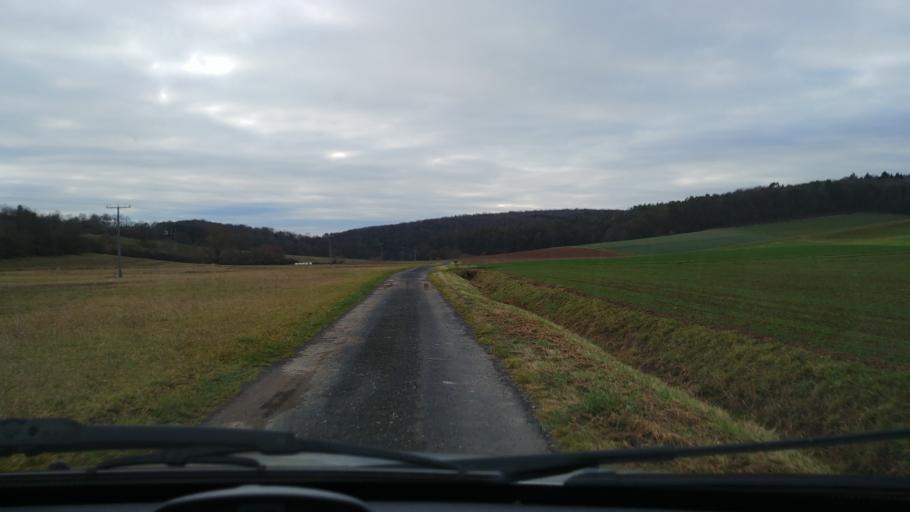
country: DE
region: Bavaria
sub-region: Regierungsbezirk Unterfranken
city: Arnstein
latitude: 50.0063
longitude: 9.9904
